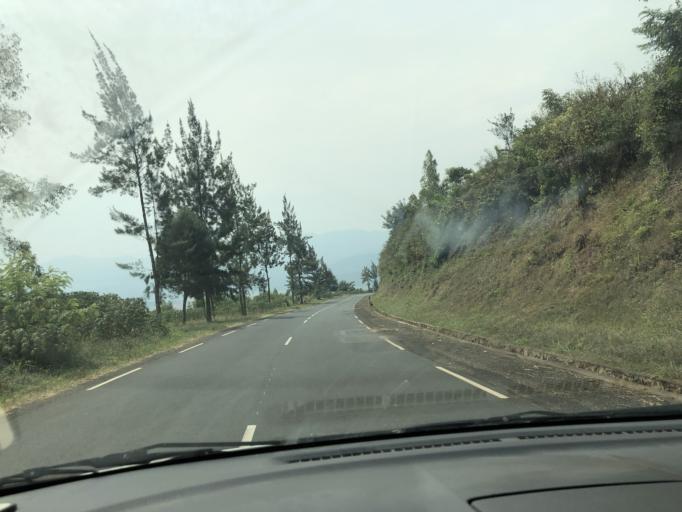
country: RW
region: Western Province
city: Cyangugu
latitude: -2.6679
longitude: 28.9978
